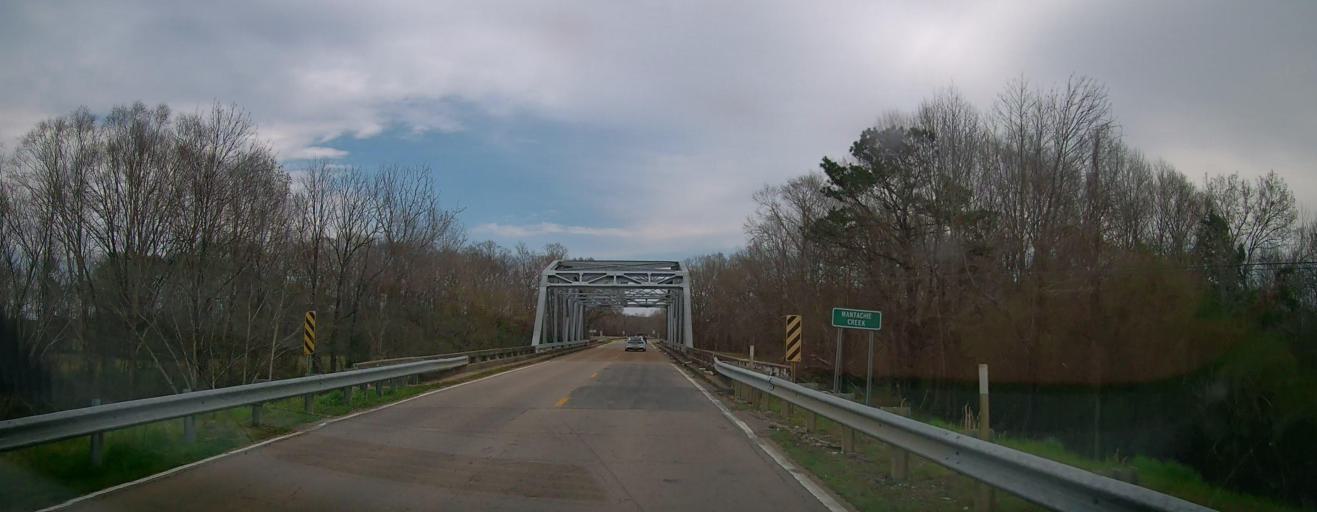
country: US
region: Mississippi
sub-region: Itawamba County
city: Fulton
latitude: 34.2527
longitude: -88.4771
